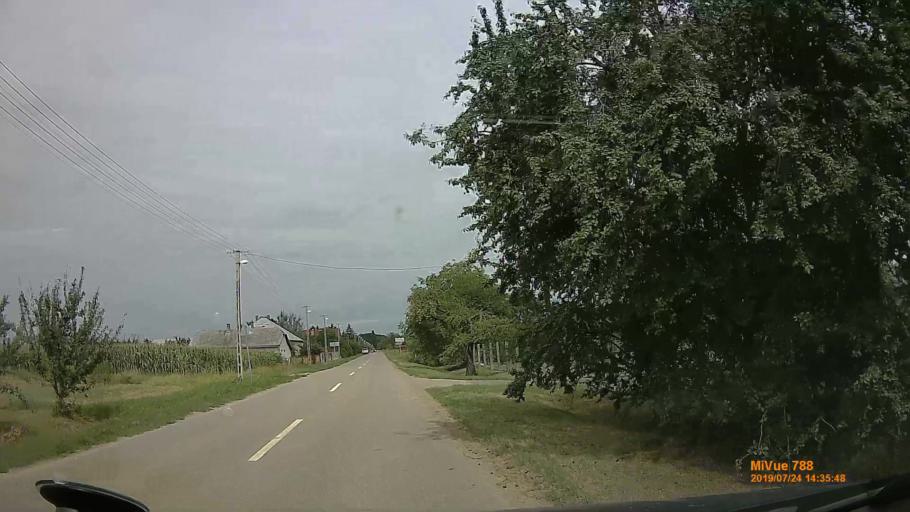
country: HU
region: Szabolcs-Szatmar-Bereg
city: Mandok
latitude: 48.3186
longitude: 22.2566
